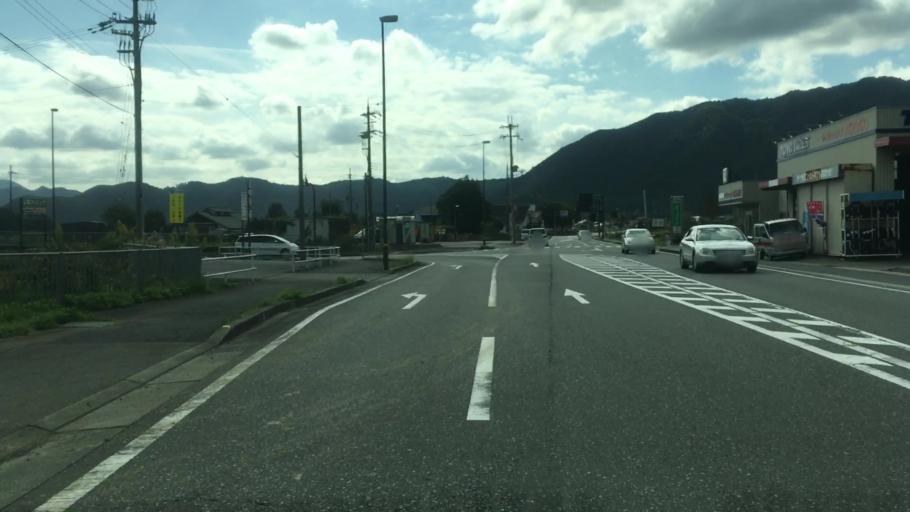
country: JP
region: Kyoto
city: Fukuchiyama
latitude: 35.2434
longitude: 135.0079
